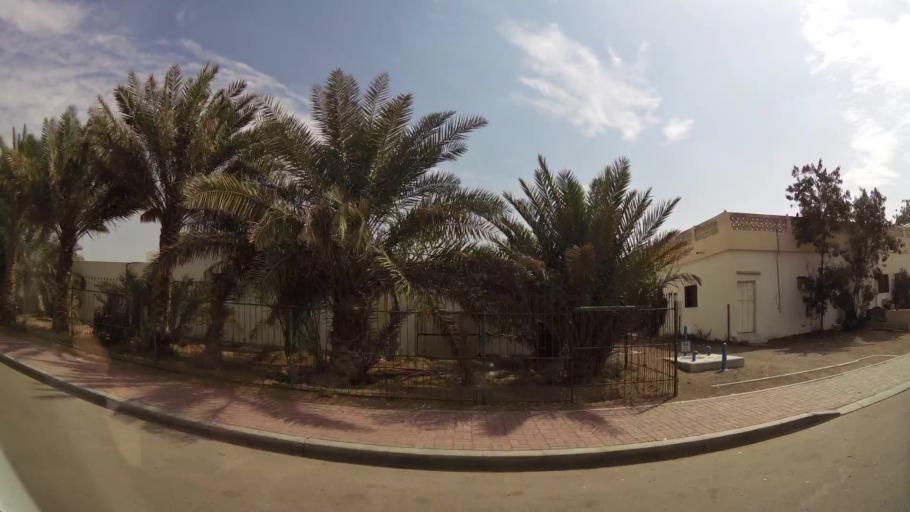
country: AE
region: Abu Dhabi
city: Al Ain
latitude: 24.1950
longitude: 55.7945
